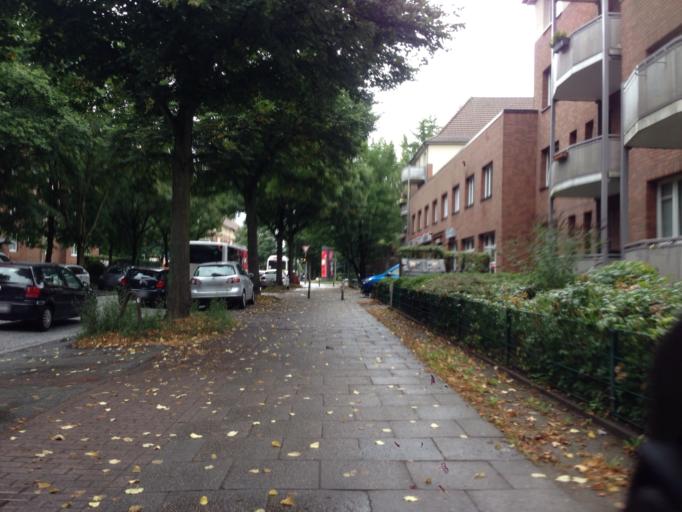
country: DE
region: Hamburg
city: Marienthal
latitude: 53.5528
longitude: 10.0877
